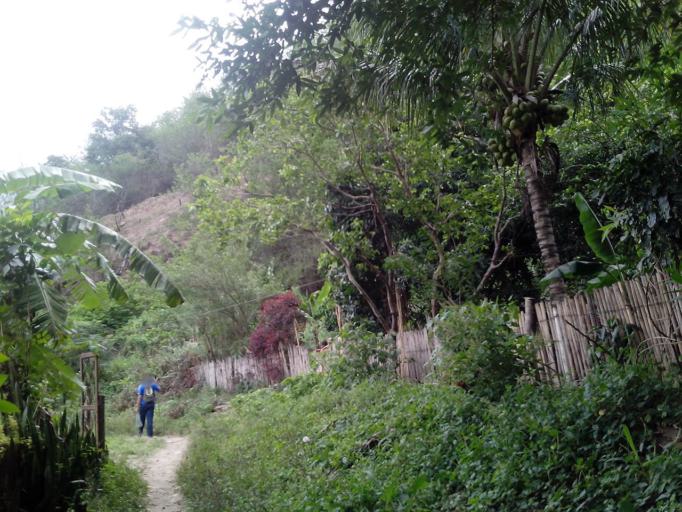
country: BR
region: Rio de Janeiro
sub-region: Miguel Pereira
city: Miguel Pereira
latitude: -22.5075
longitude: -43.5223
